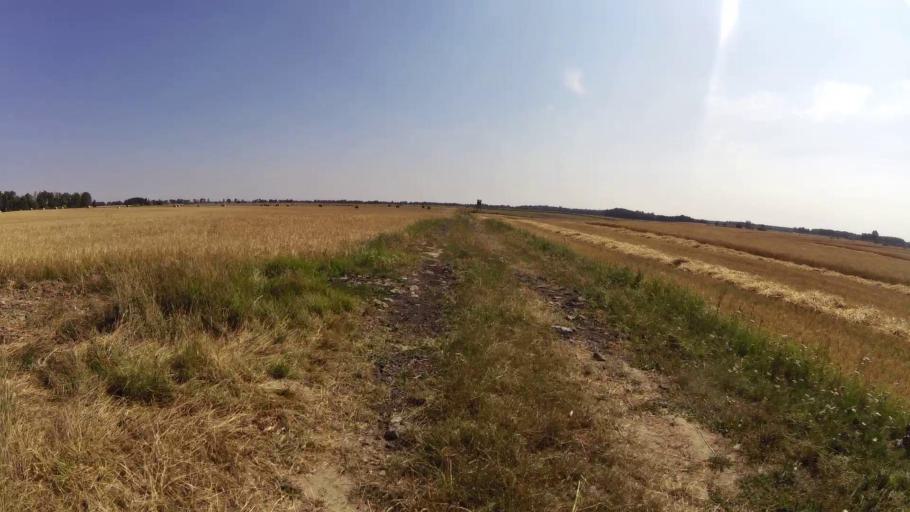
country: PL
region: West Pomeranian Voivodeship
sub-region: Powiat walecki
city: Walcz
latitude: 53.3293
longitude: 16.3143
